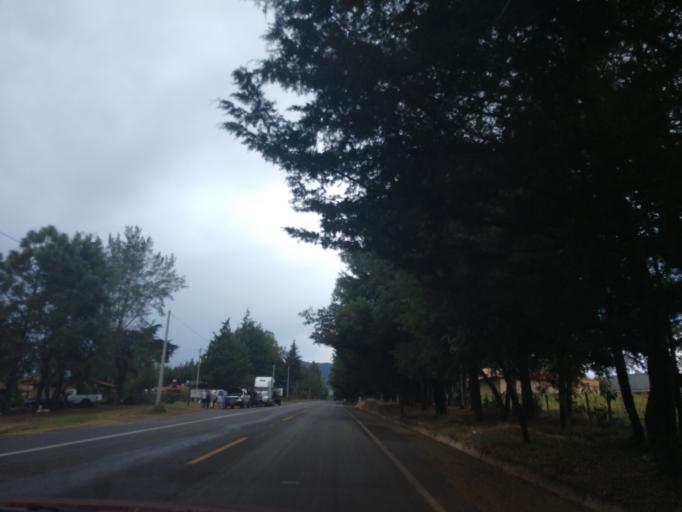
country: MX
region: Jalisco
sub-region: Mazamitla
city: Mazamitla
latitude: 19.9340
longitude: -103.0450
